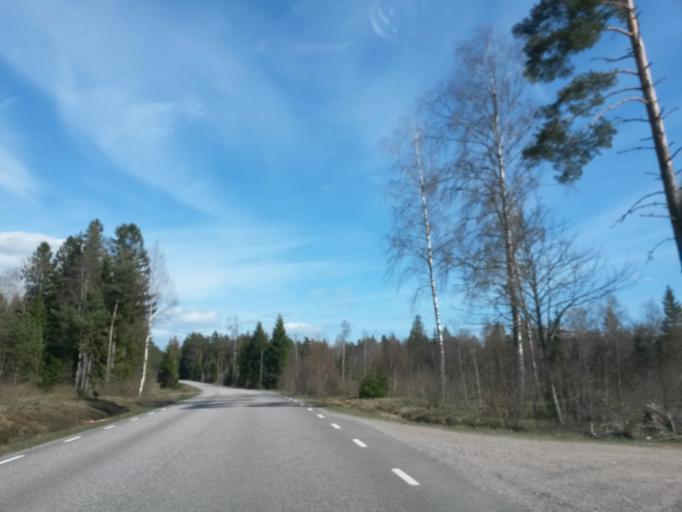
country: SE
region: Vaestra Goetaland
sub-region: Vargarda Kommun
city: Jonstorp
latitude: 57.9835
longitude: 12.7399
